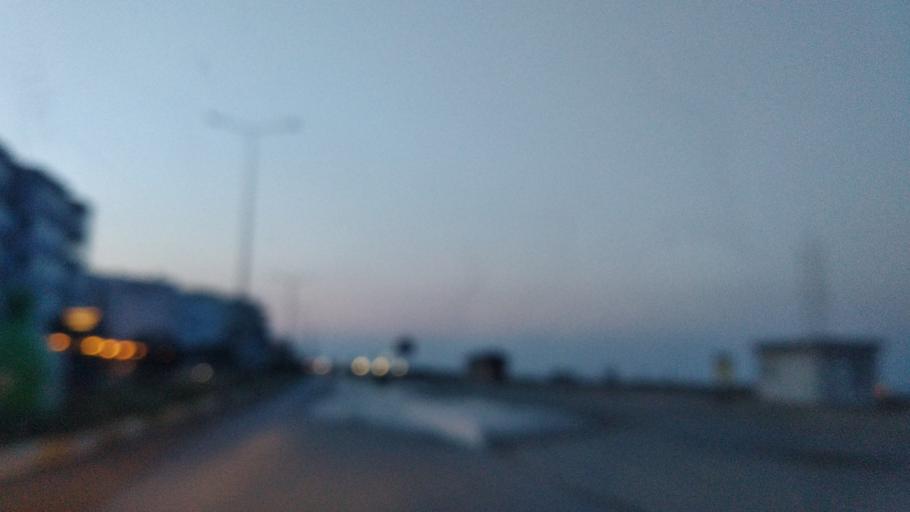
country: TR
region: Sakarya
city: Karasu
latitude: 41.1010
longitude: 30.7179
